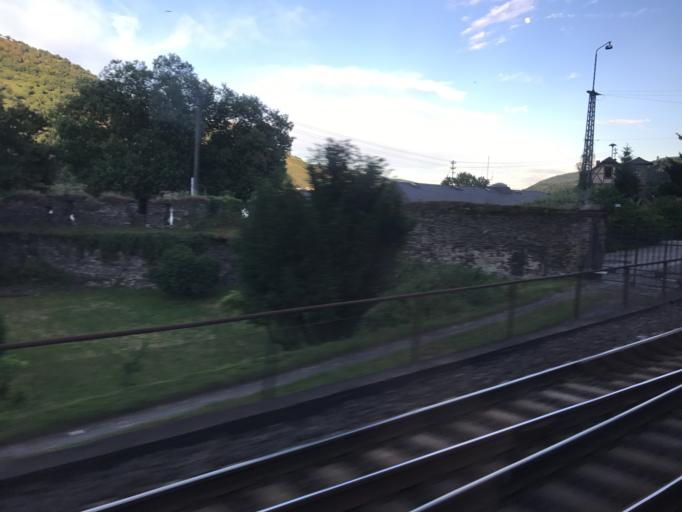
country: DE
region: Rheinland-Pfalz
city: Bacharach
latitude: 50.0569
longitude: 7.7694
